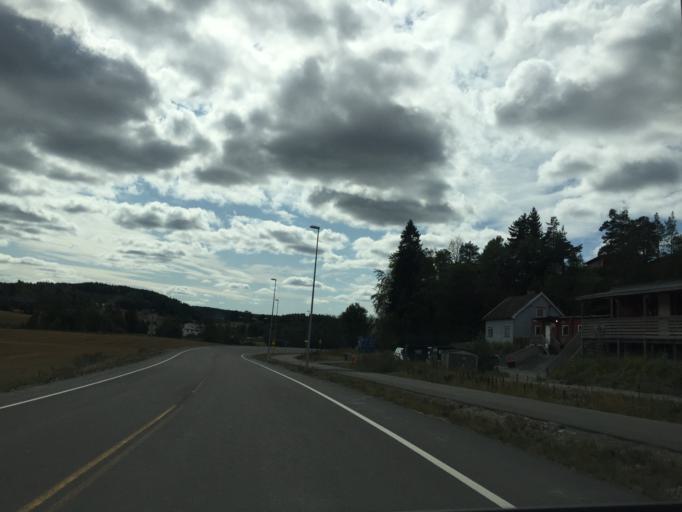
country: NO
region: Ostfold
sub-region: Hobol
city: Elvestad
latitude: 59.6267
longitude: 10.9544
